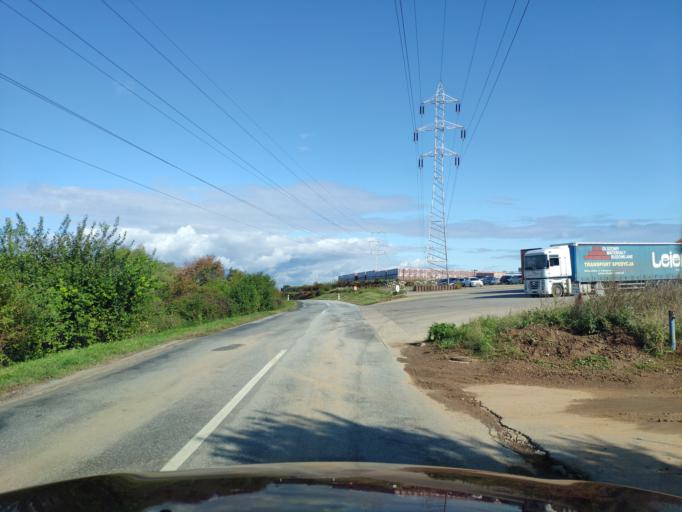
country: SK
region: Presovsky
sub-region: Okres Presov
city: Presov
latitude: 48.9047
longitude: 21.2619
